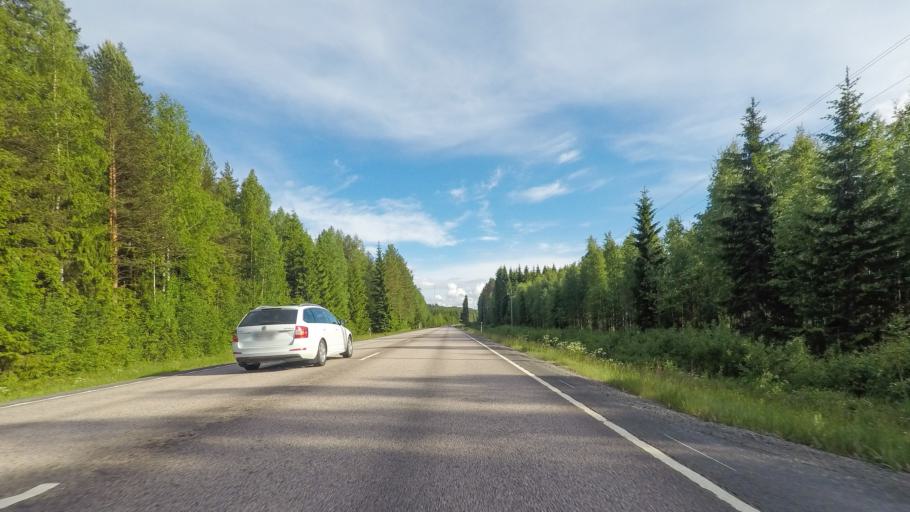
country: FI
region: Central Finland
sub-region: Joutsa
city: Leivonmaeki
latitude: 61.9395
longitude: 26.1127
